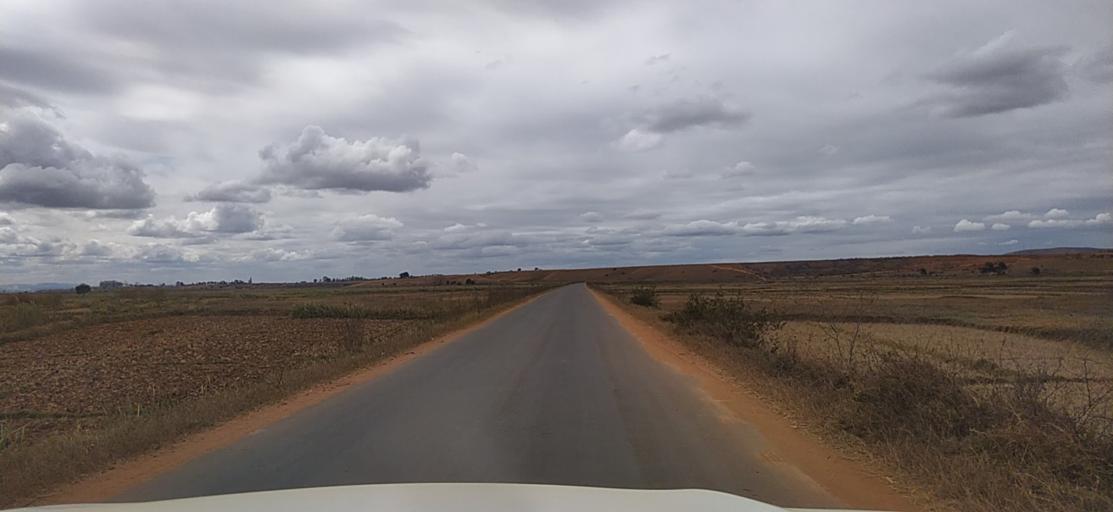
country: MG
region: Alaotra Mangoro
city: Ambatondrazaka
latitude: -17.9209
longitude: 48.2577
